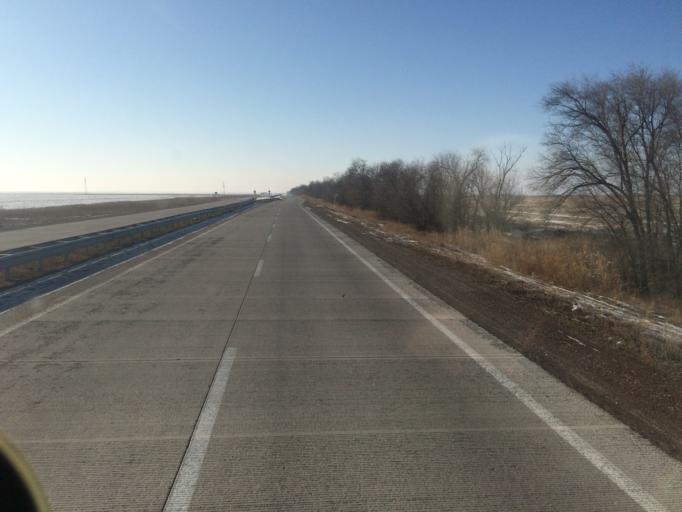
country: KG
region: Chuy
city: Belovodskoye
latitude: 43.2162
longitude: 74.1337
